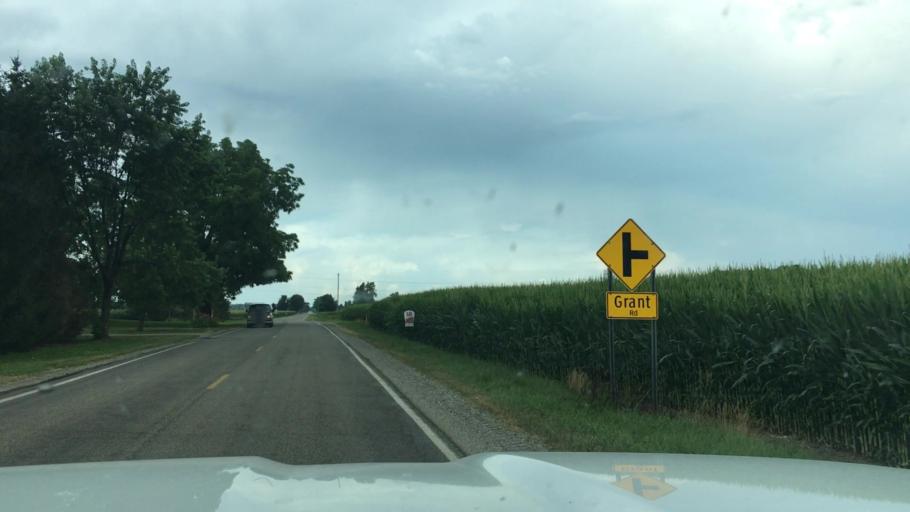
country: US
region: Michigan
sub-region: Montcalm County
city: Carson City
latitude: 43.2036
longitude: -84.7779
